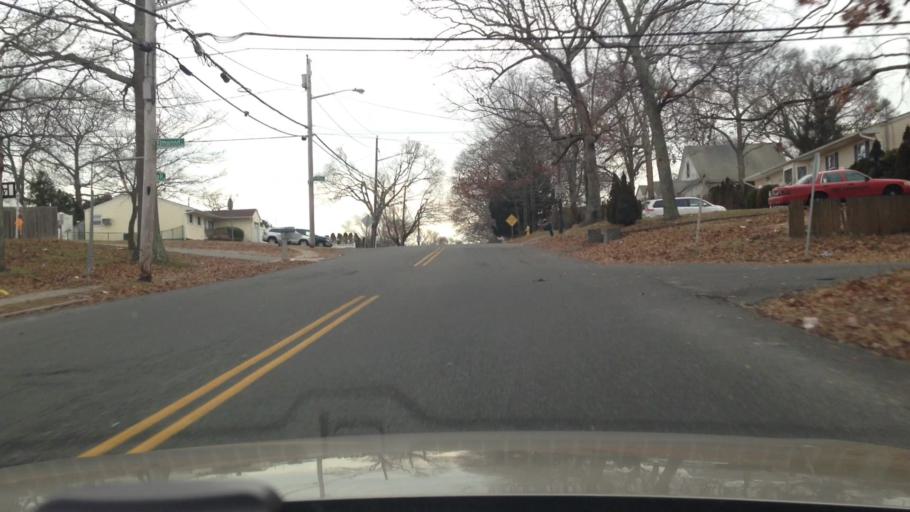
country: US
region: New York
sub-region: Suffolk County
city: Selden
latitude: 40.8627
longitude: -73.0348
